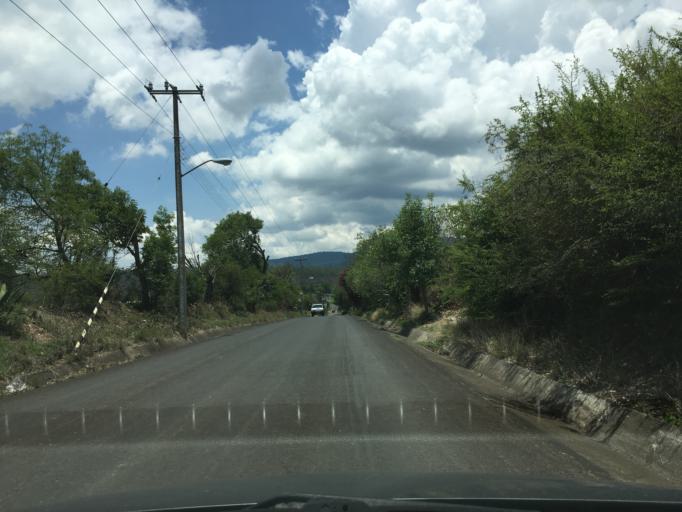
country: MX
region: Michoacan
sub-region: Morelia
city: La Mintzita (Piedra Dura)
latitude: 19.5914
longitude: -101.2737
